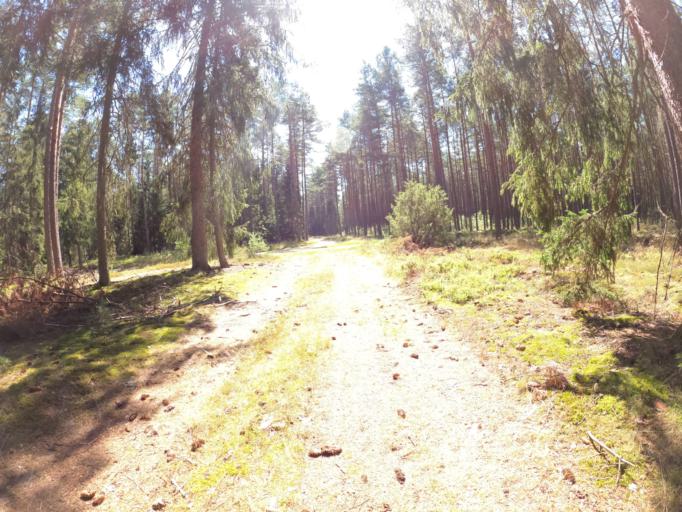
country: PL
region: West Pomeranian Voivodeship
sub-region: Powiat bialogardzki
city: Tychowo
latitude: 54.0605
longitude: 16.3679
